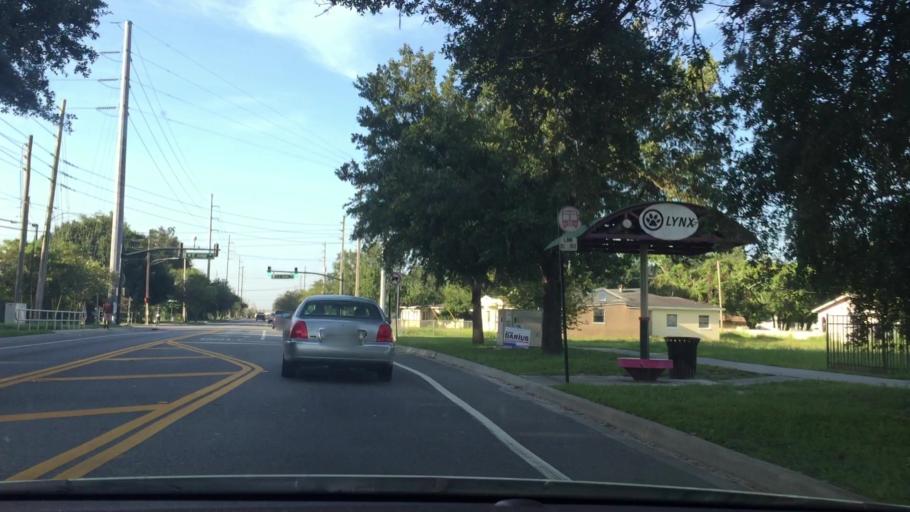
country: US
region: Florida
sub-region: Orange County
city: Pine Hills
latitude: 28.5607
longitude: -81.4306
